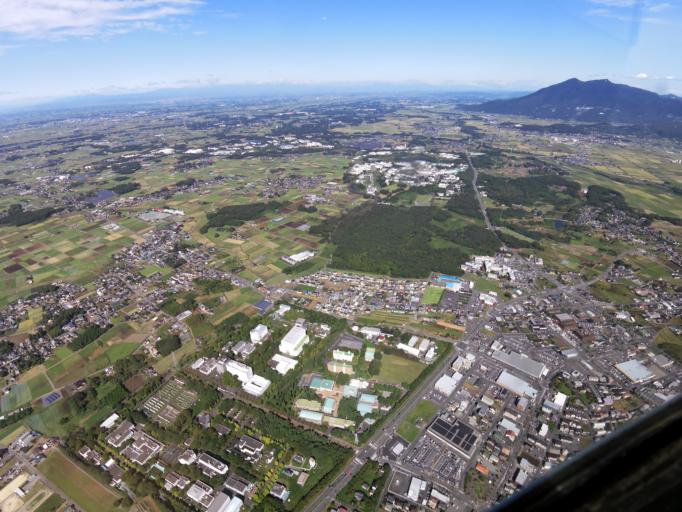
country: JP
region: Ibaraki
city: Tsukuba
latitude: 36.1281
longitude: 140.0790
